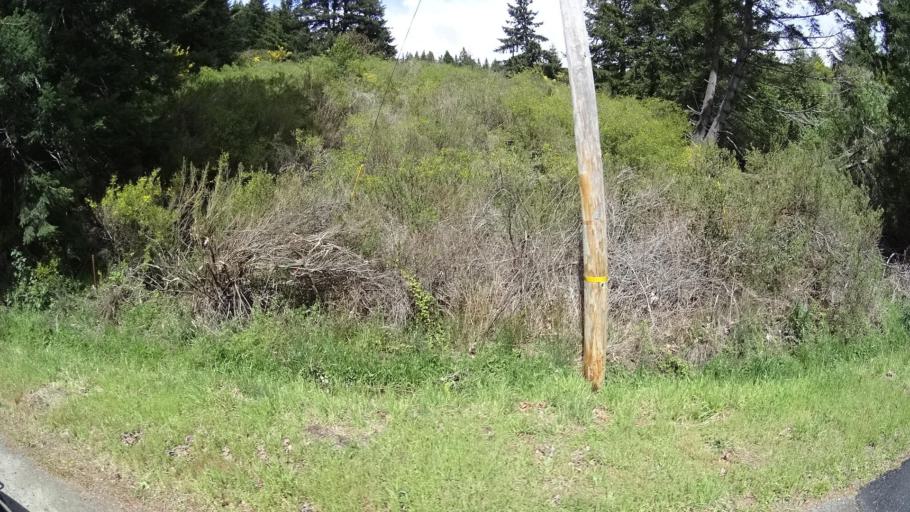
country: US
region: California
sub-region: Humboldt County
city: Blue Lake
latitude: 40.7661
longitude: -123.9438
